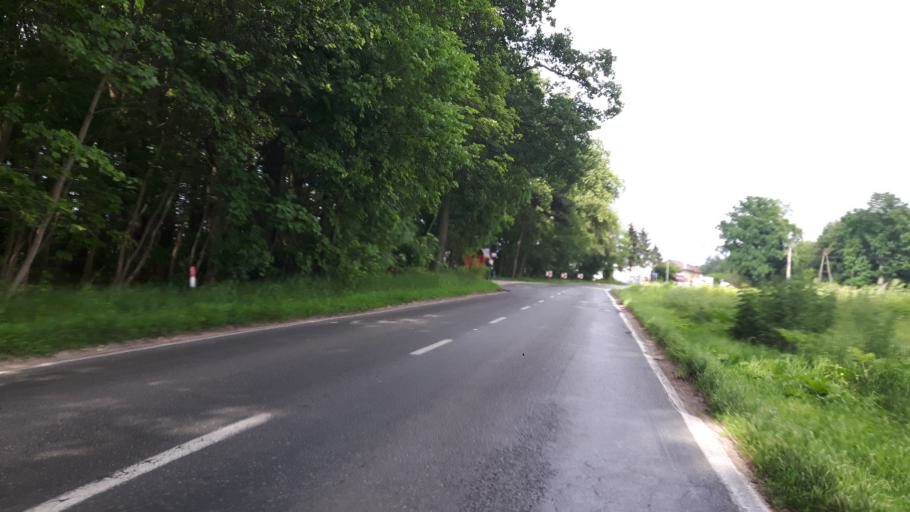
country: PL
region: West Pomeranian Voivodeship
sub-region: Powiat gryfinski
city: Stare Czarnowo
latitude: 53.4266
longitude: 14.7166
